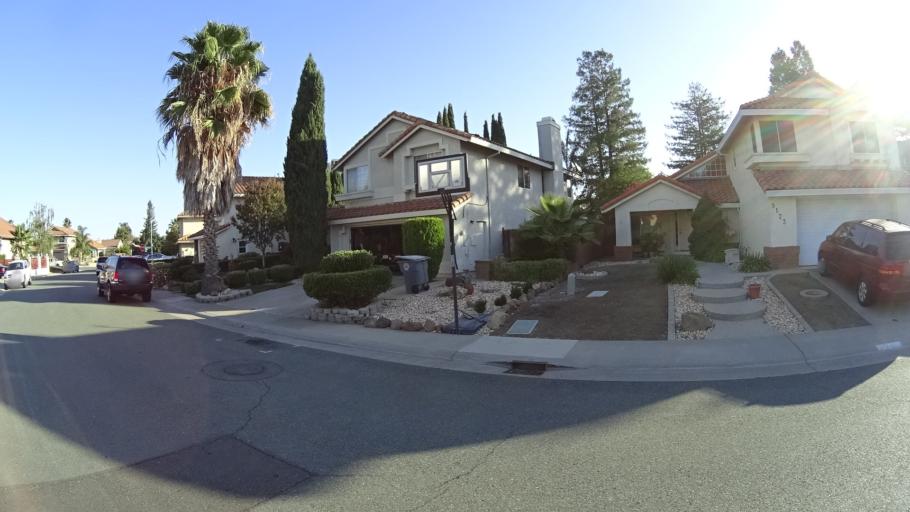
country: US
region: California
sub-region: Sacramento County
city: Laguna
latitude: 38.4260
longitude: -121.4508
